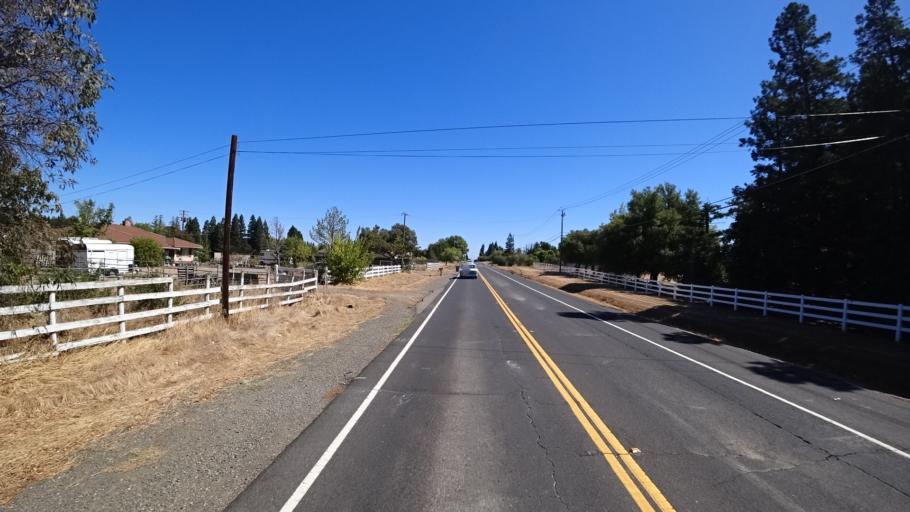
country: US
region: California
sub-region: Sacramento County
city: Elk Grove
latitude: 38.4381
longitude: -121.3664
